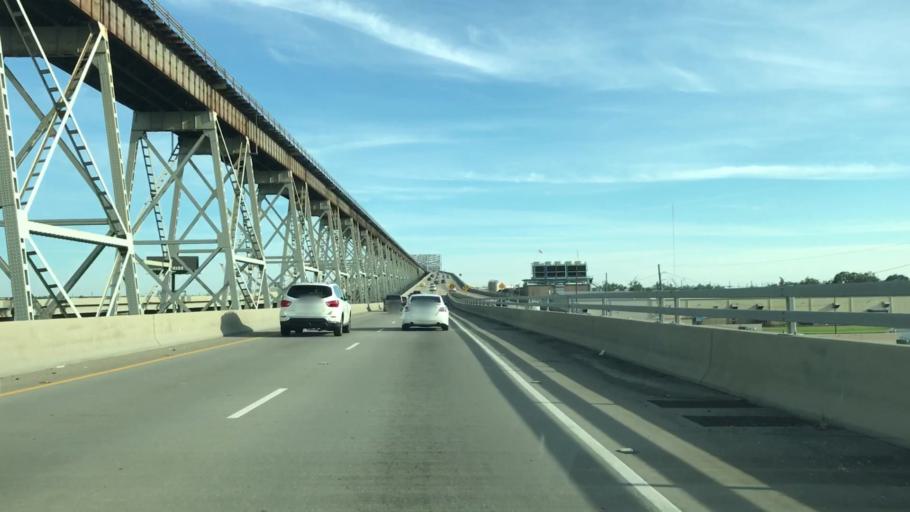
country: US
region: Louisiana
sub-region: Jefferson Parish
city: Elmwood
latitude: 29.9523
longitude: -90.1789
